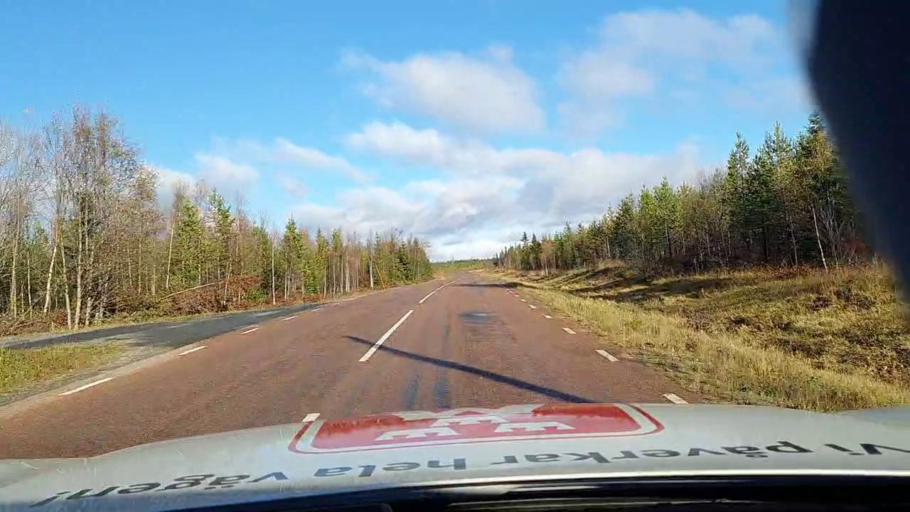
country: SE
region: Jaemtland
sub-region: Krokoms Kommun
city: Valla
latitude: 63.1666
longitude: 13.9946
